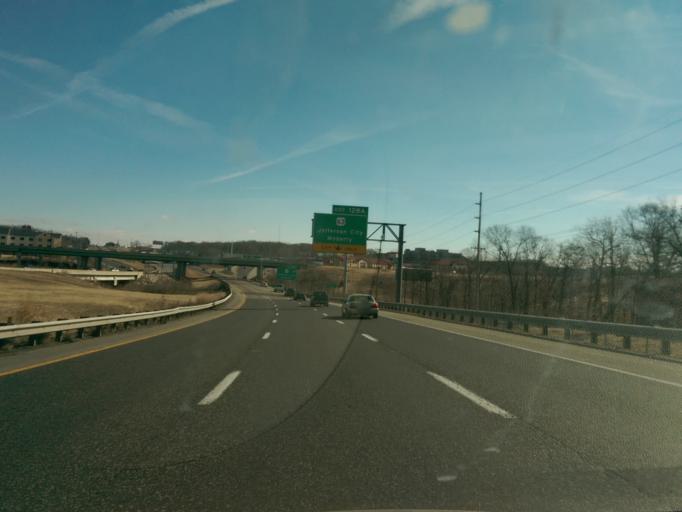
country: US
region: Missouri
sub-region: Boone County
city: Columbia
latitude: 38.9628
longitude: -92.2982
